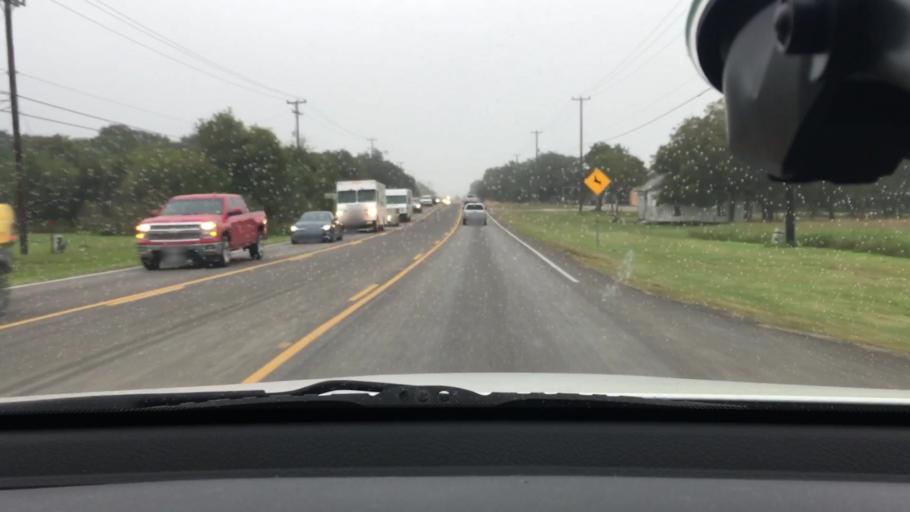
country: US
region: Texas
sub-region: Comal County
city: Garden Ridge
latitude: 29.6135
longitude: -98.3187
